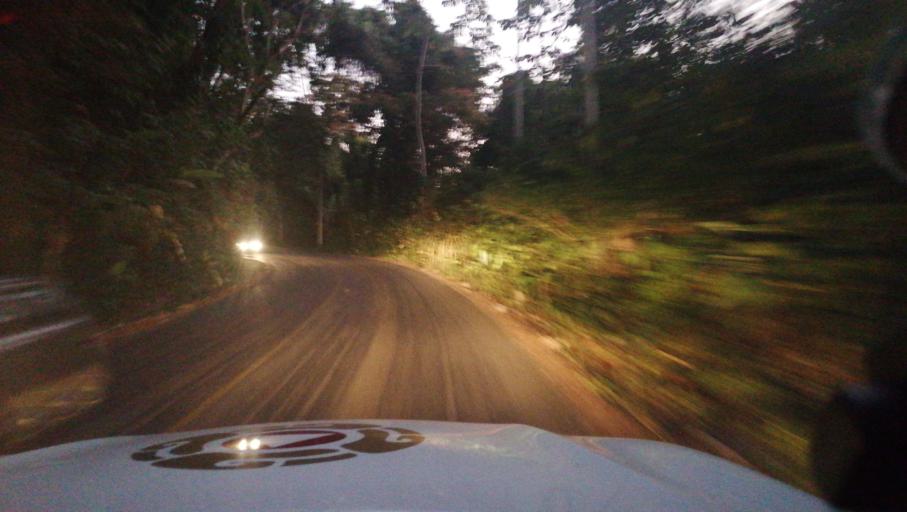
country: MX
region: Chiapas
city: Veinte de Noviembre
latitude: 14.9669
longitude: -92.2528
